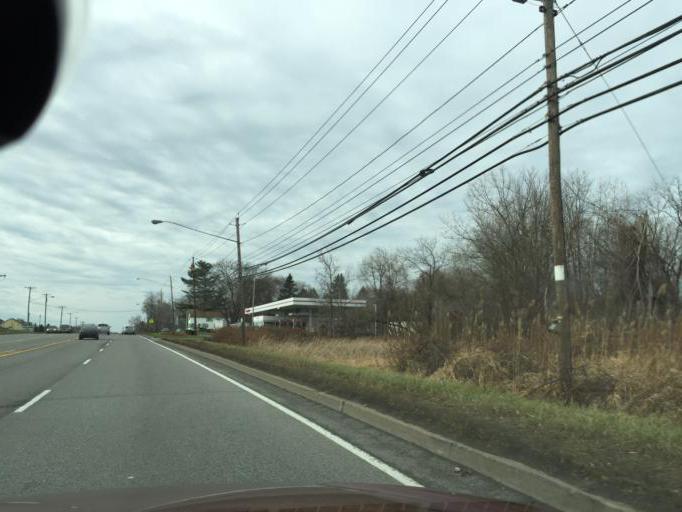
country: US
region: New York
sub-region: Monroe County
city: Rochester
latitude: 43.0931
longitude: -77.6560
